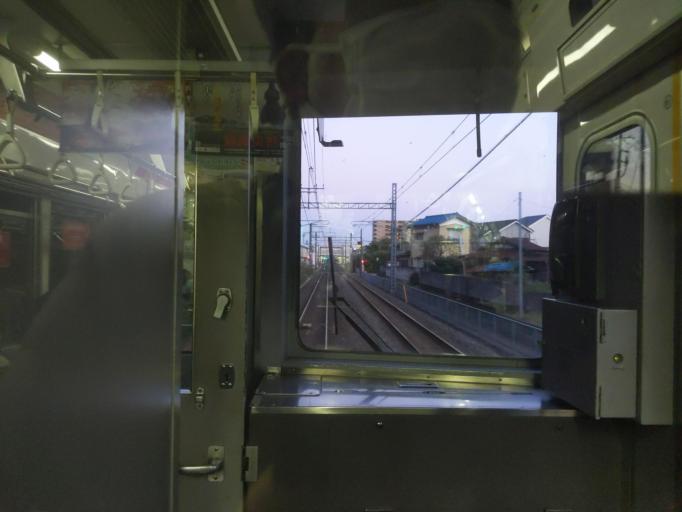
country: JP
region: Chiba
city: Kashiwa
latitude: 35.8679
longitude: 139.9361
